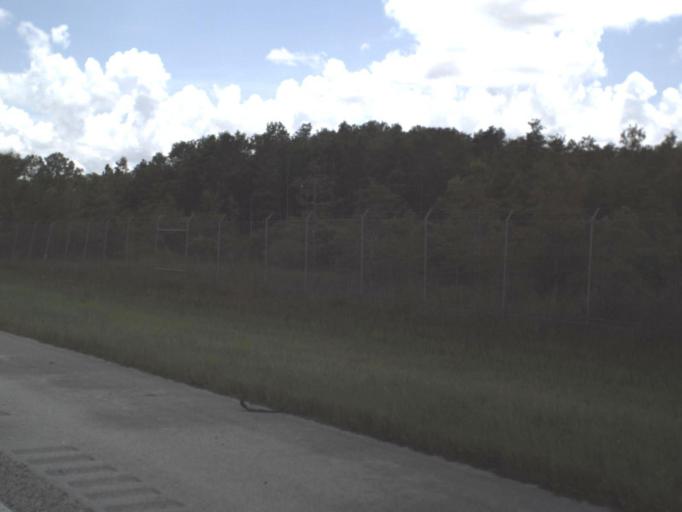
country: US
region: Florida
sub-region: Collier County
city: Immokalee
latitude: 26.1709
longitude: -80.9573
